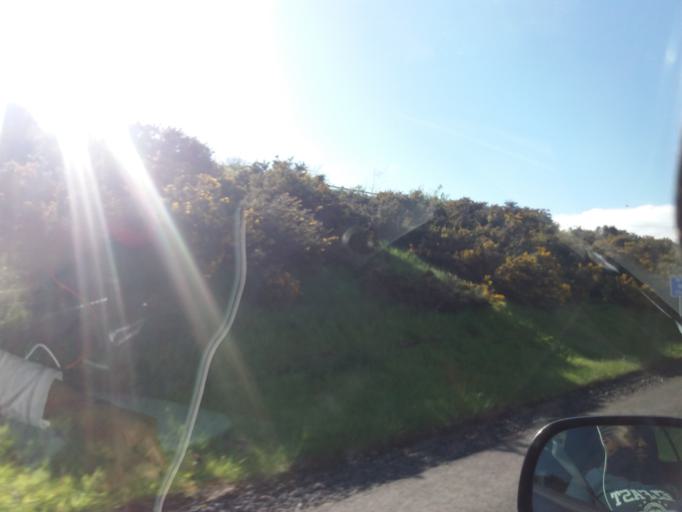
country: IE
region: Munster
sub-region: Waterford
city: Waterford
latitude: 52.3236
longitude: -7.1473
